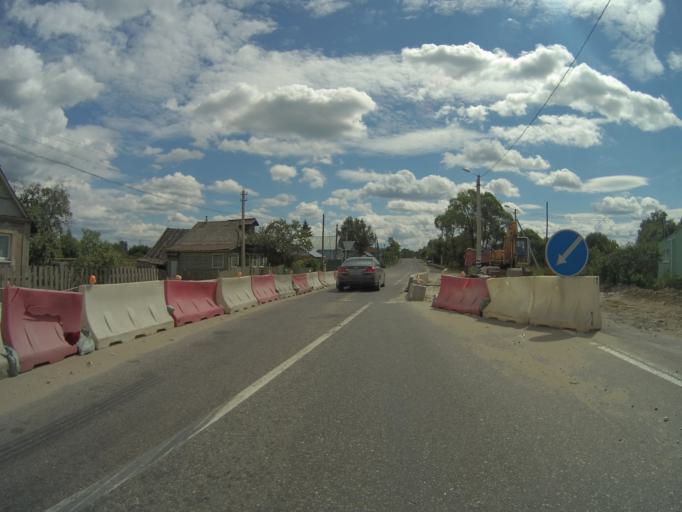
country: RU
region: Vladimir
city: Kommunar
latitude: 56.0408
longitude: 40.5475
